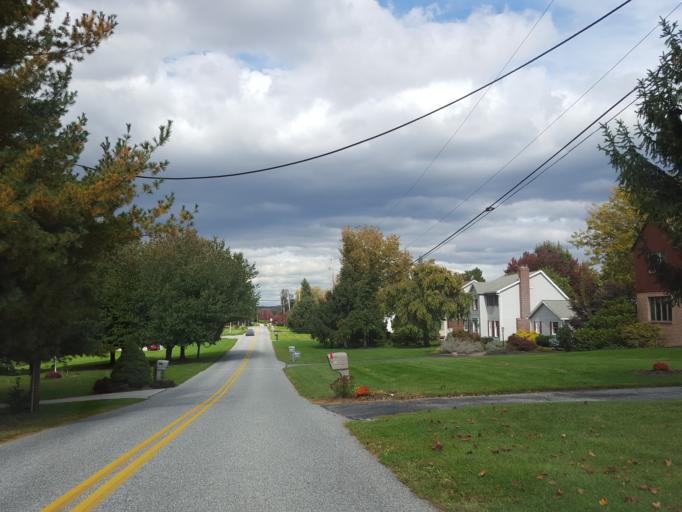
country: US
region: Pennsylvania
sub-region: York County
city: Spry
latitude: 39.9278
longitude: -76.6725
